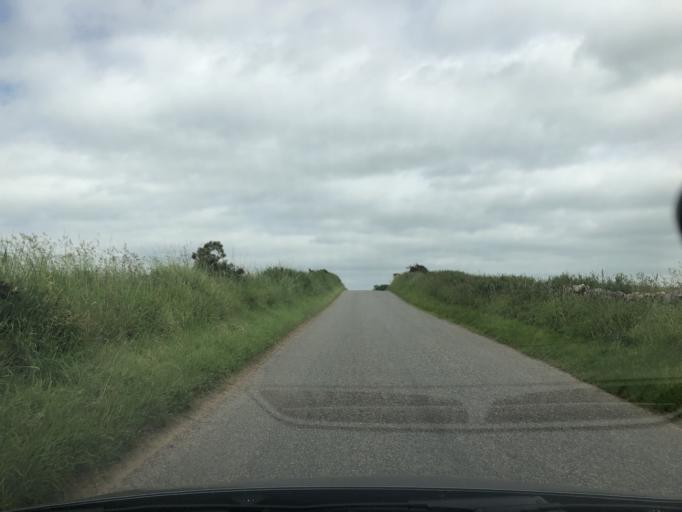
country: GB
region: Scotland
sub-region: Angus
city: Forfar
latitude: 56.7245
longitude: -2.9160
